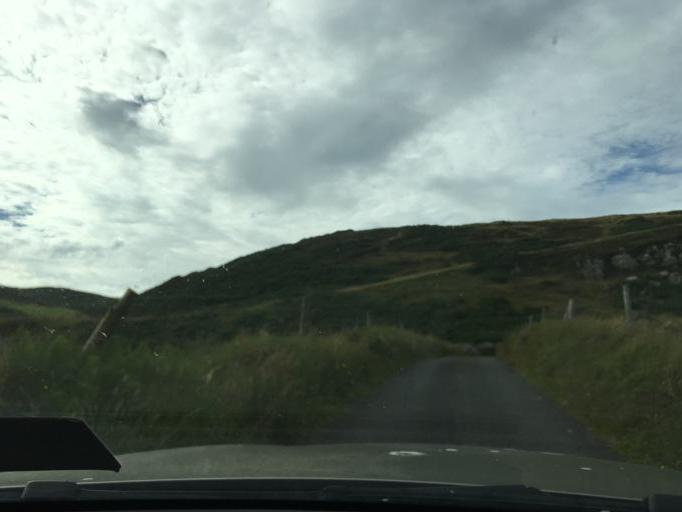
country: IE
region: Ulster
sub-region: County Donegal
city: Carndonagh
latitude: 55.3295
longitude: -7.3200
